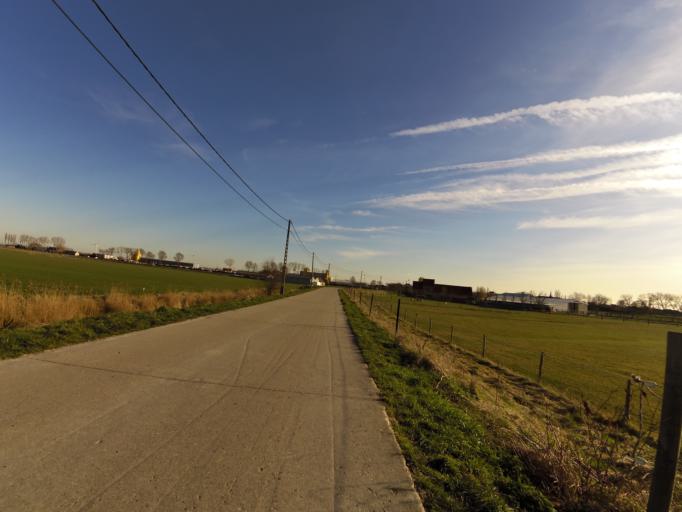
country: BE
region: Flanders
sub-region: Provincie West-Vlaanderen
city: Gistel
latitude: 51.1825
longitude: 2.9405
